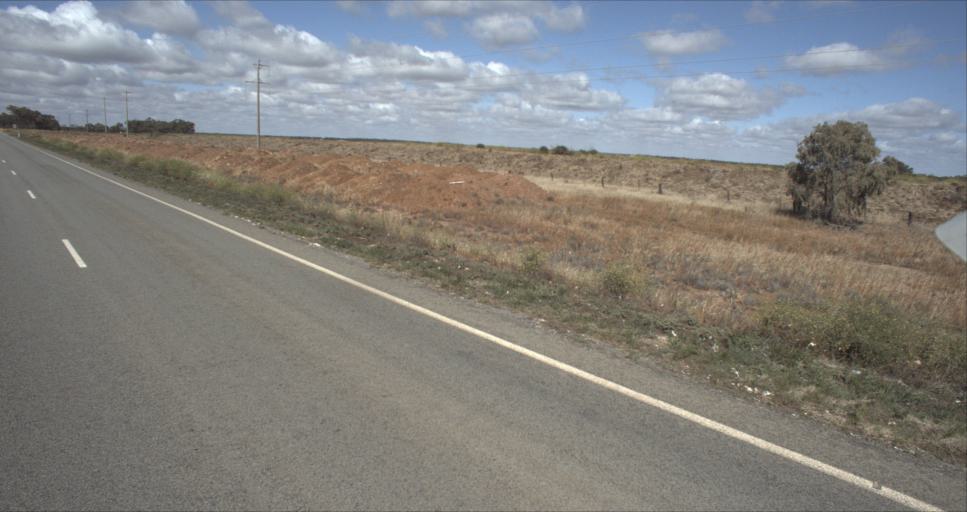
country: AU
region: New South Wales
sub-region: Murrumbidgee Shire
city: Darlington Point
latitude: -34.5502
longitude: 146.1707
